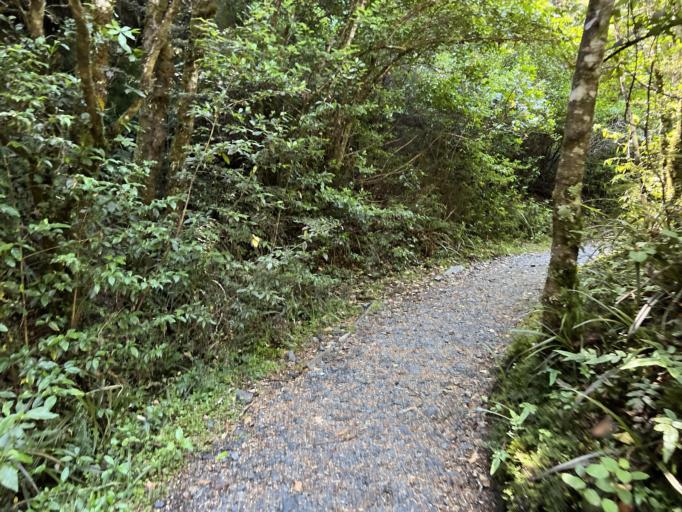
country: NZ
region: Manawatu-Wanganui
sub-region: Ruapehu District
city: Waiouru
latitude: -39.2016
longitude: 175.5482
